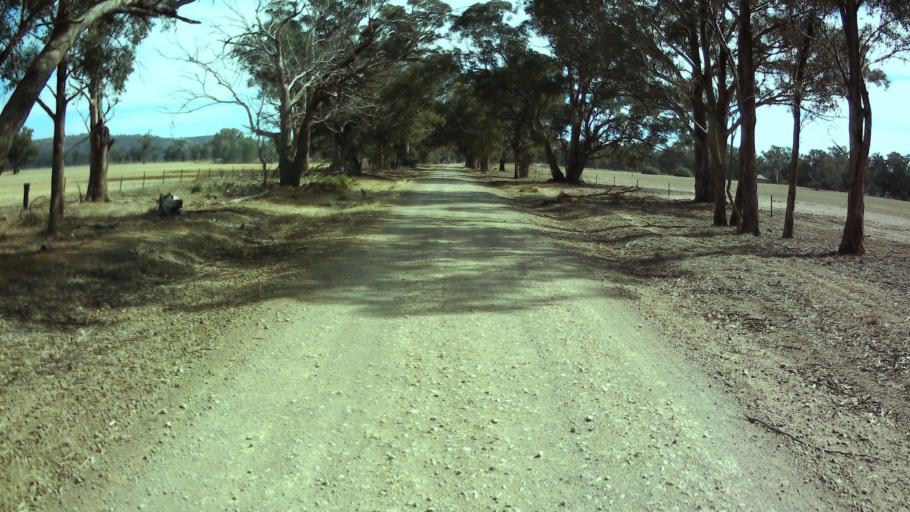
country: AU
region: New South Wales
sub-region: Weddin
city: Grenfell
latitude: -33.6967
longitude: 148.3028
